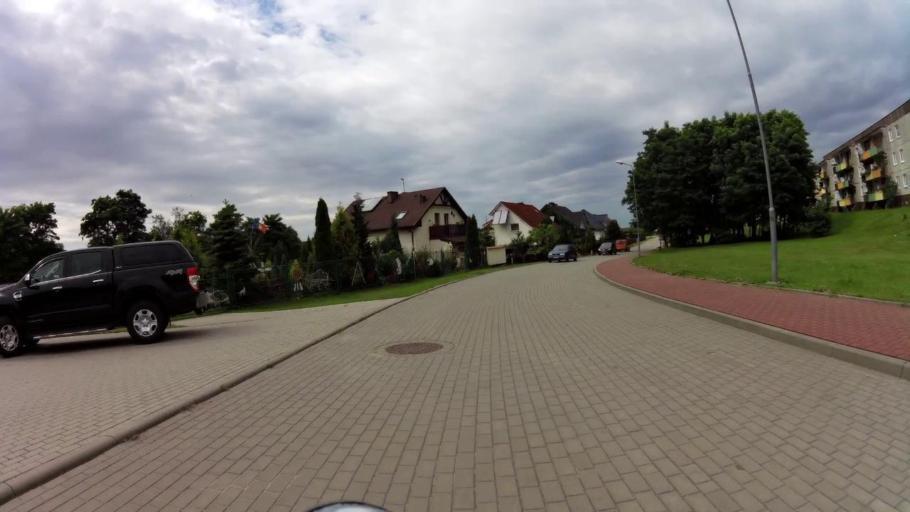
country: PL
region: West Pomeranian Voivodeship
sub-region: Powiat bialogardzki
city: Karlino
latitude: 54.0411
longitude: 15.8707
